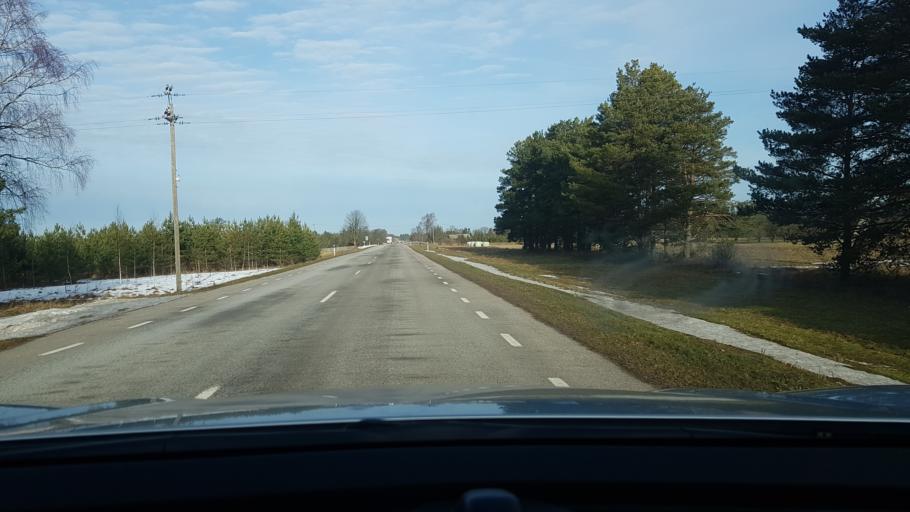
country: EE
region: Saare
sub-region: Kuressaare linn
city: Kuressaare
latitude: 58.5154
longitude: 22.7043
